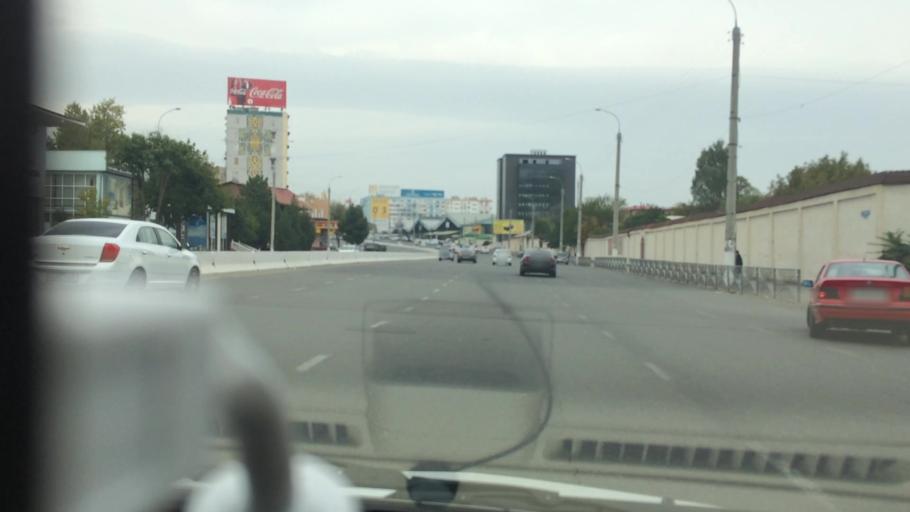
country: UZ
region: Toshkent
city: Salor
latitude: 41.3163
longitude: 69.3180
